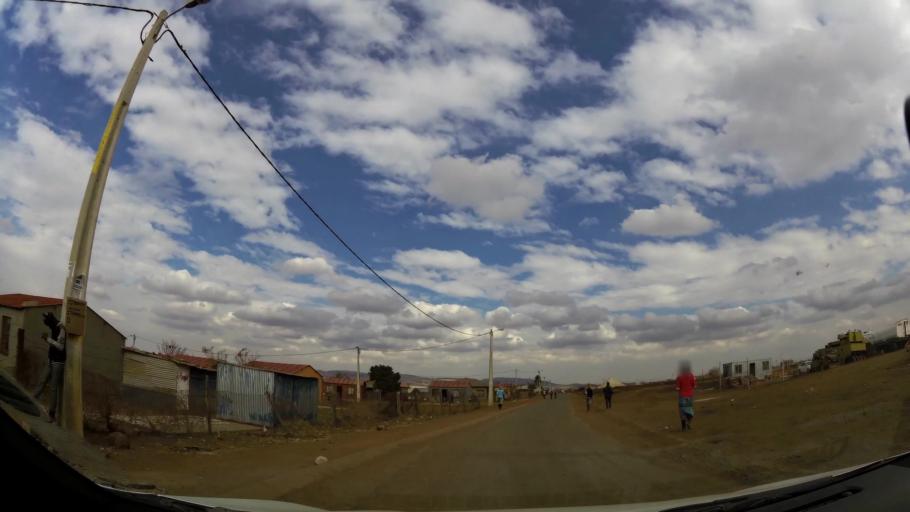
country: ZA
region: Gauteng
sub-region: Ekurhuleni Metropolitan Municipality
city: Germiston
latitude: -26.4053
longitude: 28.1613
